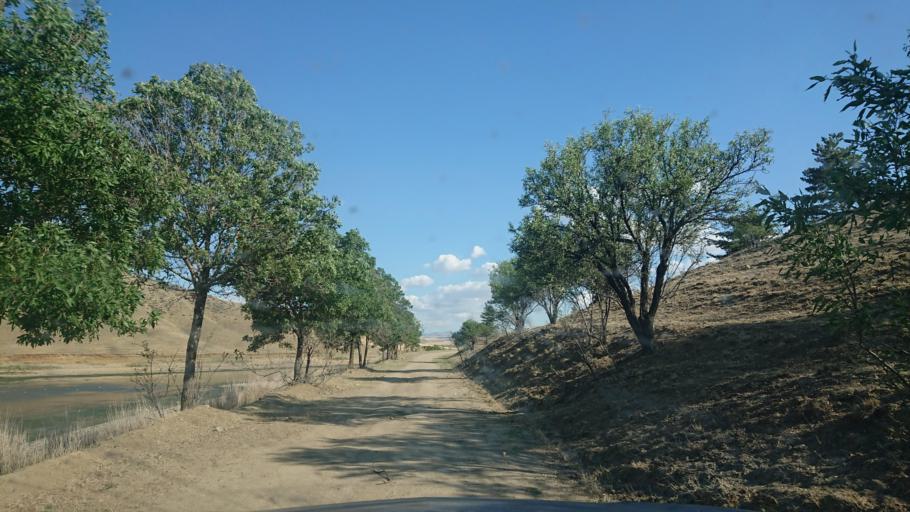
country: TR
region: Aksaray
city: Sariyahsi
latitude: 39.0213
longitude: 33.8962
